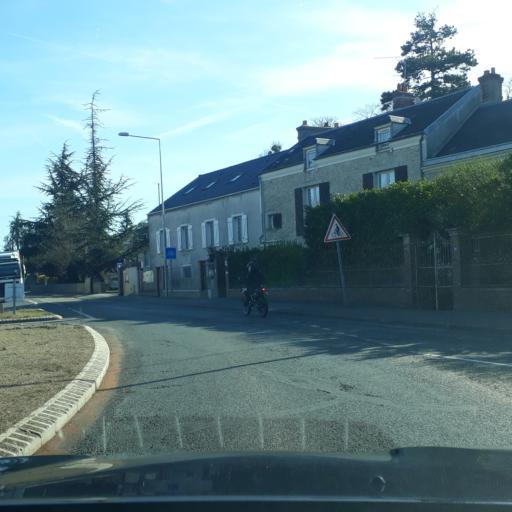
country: FR
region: Ile-de-France
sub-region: Departement de l'Essonne
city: La Ferte-Alais
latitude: 48.4889
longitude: 2.3544
